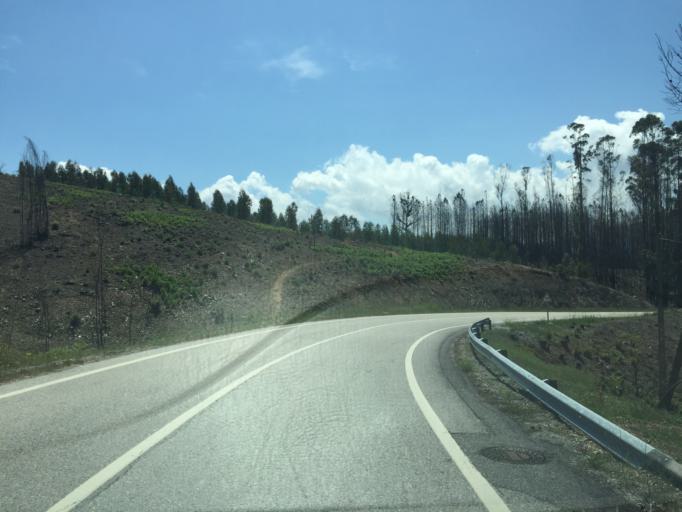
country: PT
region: Coimbra
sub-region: Pampilhosa da Serra
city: Pampilhosa da Serra
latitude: 40.0002
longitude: -7.9752
